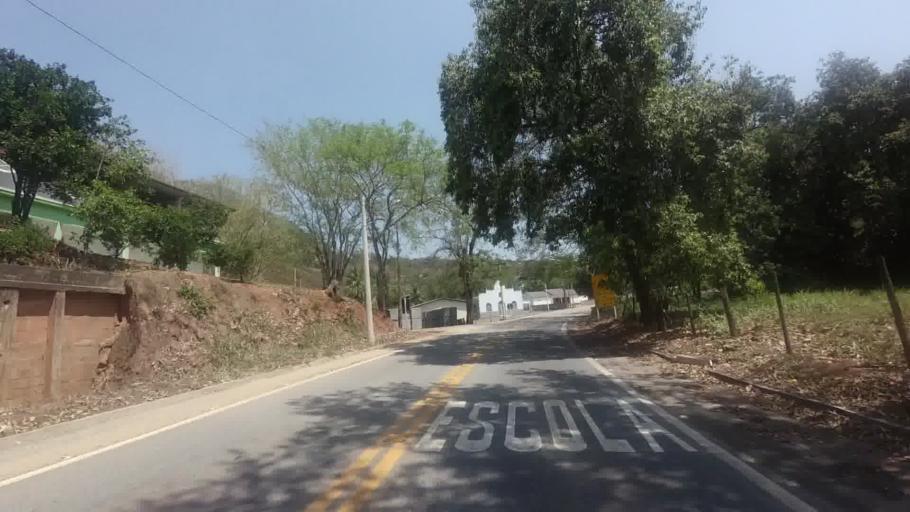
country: BR
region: Espirito Santo
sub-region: Cachoeiro De Itapemirim
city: Cachoeiro de Itapemirim
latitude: -20.8369
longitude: -41.2278
